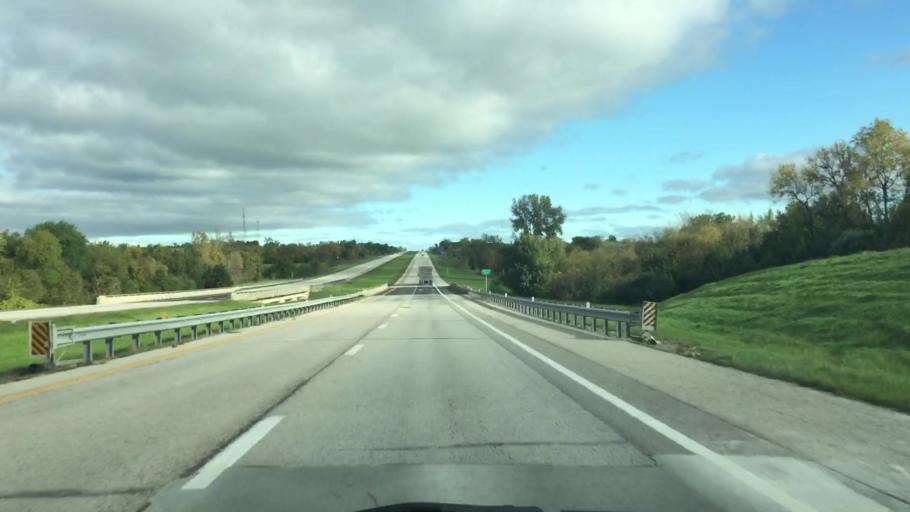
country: US
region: Missouri
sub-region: Harrison County
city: Bethany
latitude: 40.2311
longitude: -94.0127
